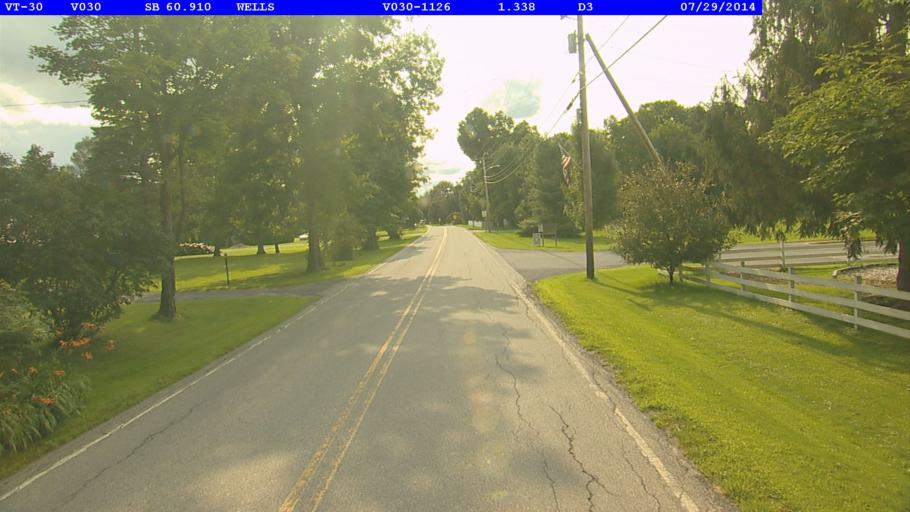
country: US
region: New York
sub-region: Washington County
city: Granville
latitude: 43.4173
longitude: -73.2067
